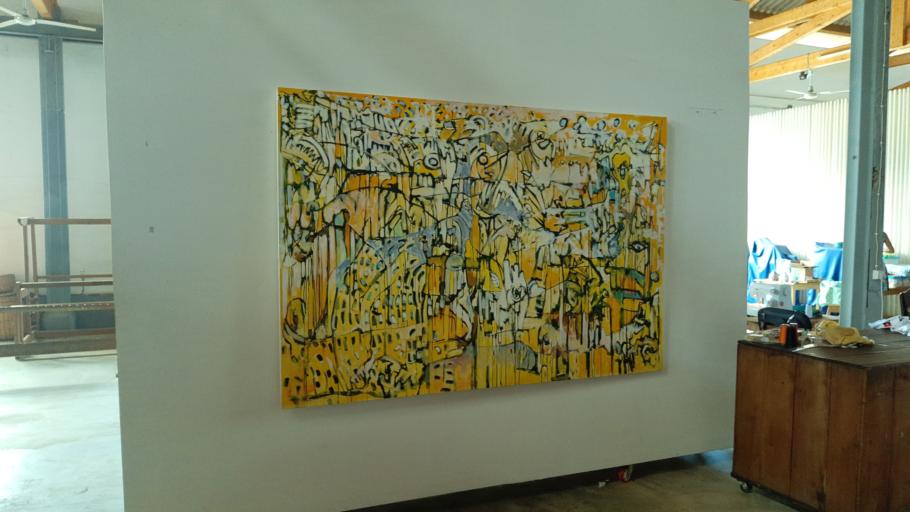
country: ST
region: Sao Tome Island
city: Sao Tome
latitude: 0.3438
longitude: 6.7372
